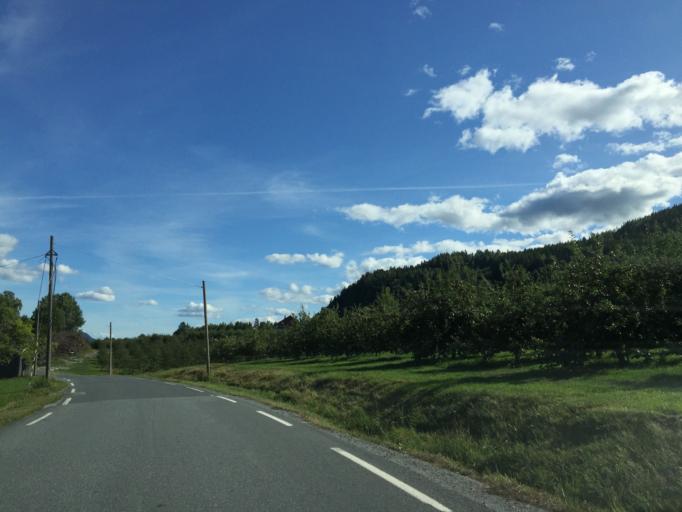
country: NO
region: Buskerud
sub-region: Ovre Eiker
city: Hokksund
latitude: 59.6874
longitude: 9.8501
